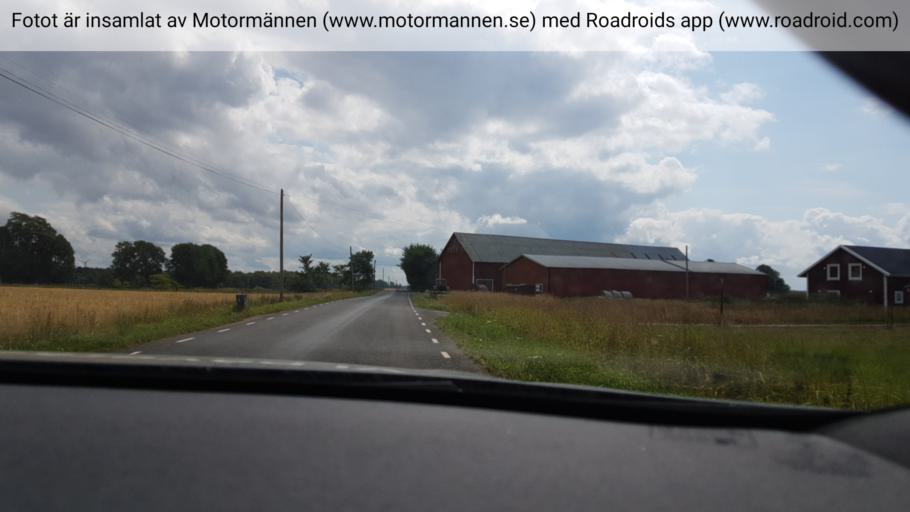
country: SE
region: Vaestra Goetaland
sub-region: Falkopings Kommun
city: Falkoeping
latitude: 58.1136
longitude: 13.4584
